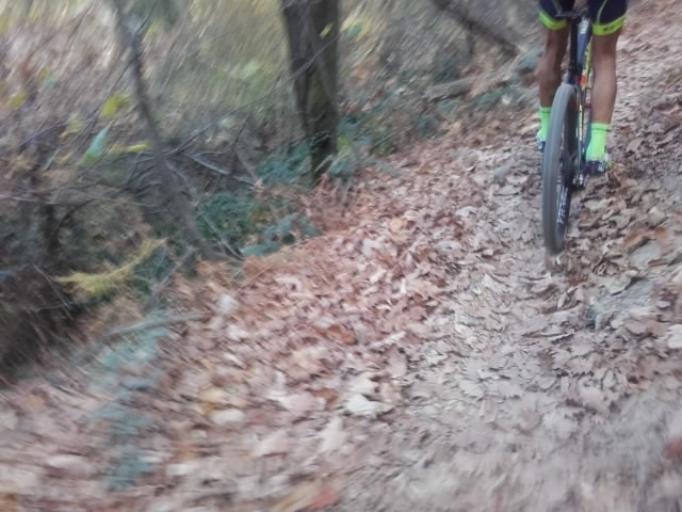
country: IT
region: Piedmont
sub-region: Provincia di Torino
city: Pino Torinese
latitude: 45.0702
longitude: 7.7812
